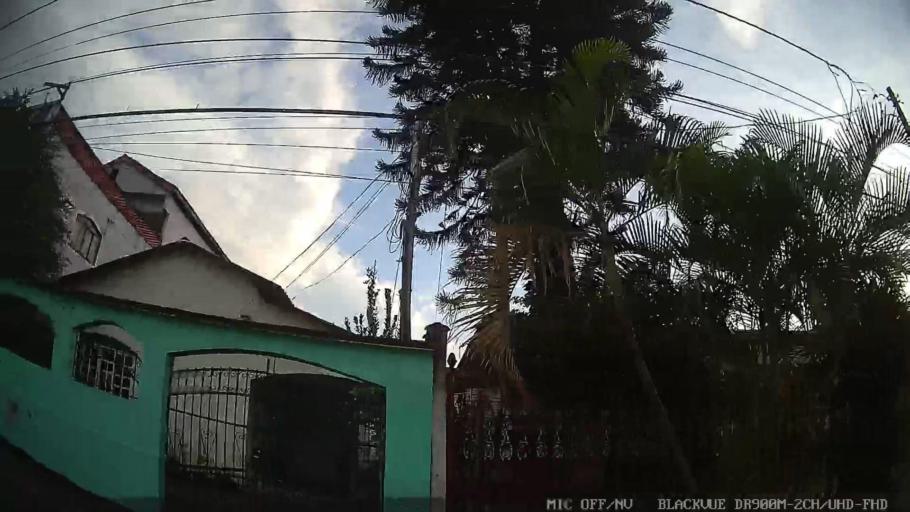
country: BR
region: Sao Paulo
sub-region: Cubatao
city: Cubatao
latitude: -23.8954
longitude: -46.4308
